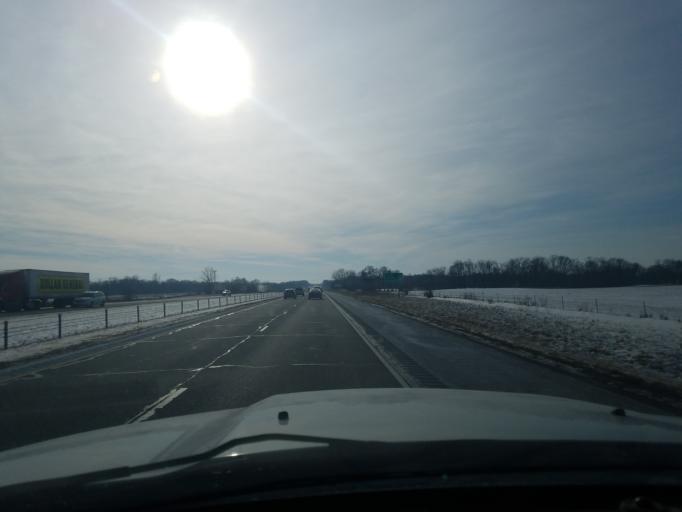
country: US
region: Indiana
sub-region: Huntington County
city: Warren
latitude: 40.7137
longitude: -85.4451
